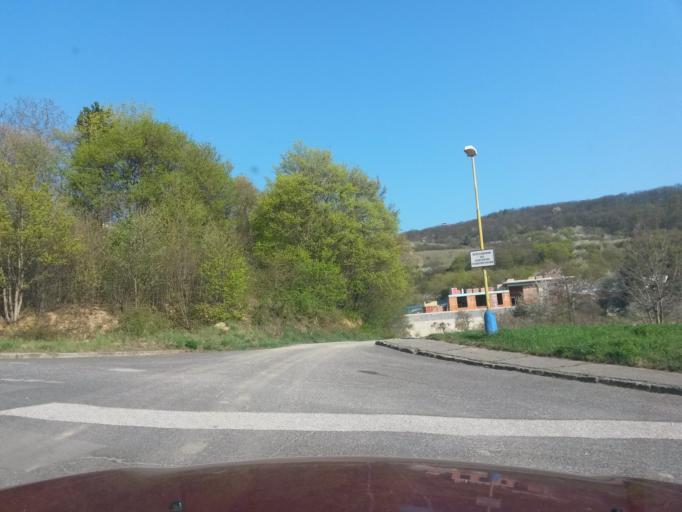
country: SK
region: Kosicky
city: Kosice
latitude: 48.7531
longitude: 21.2425
